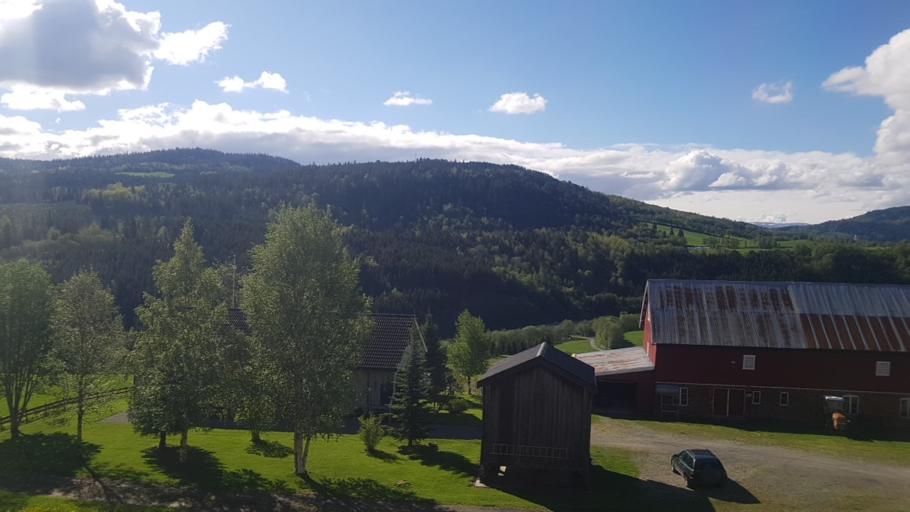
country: NO
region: Sor-Trondelag
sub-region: Midtre Gauldal
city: Storen
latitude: 62.9666
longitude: 10.1972
